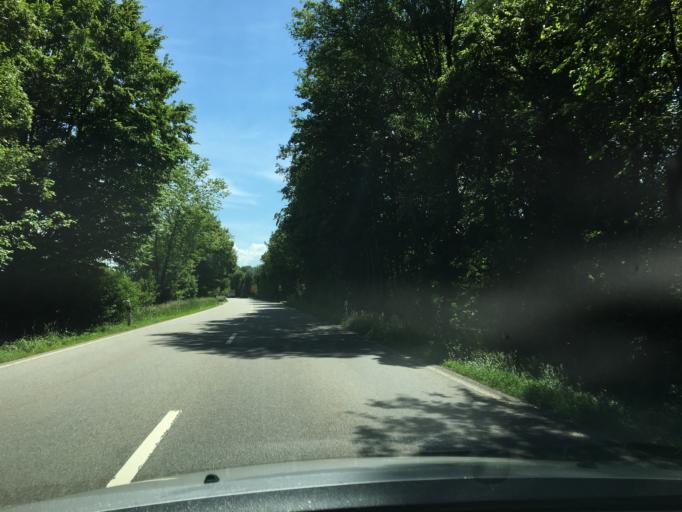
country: DE
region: Bavaria
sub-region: Upper Bavaria
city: Freilassing
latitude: 47.8589
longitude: 12.9823
